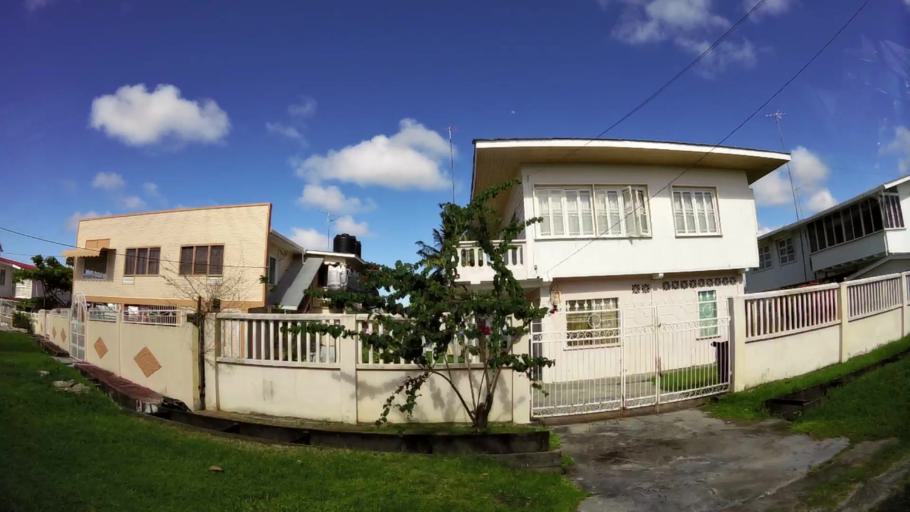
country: GY
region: Demerara-Mahaica
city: Georgetown
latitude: 6.8166
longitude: -58.1293
